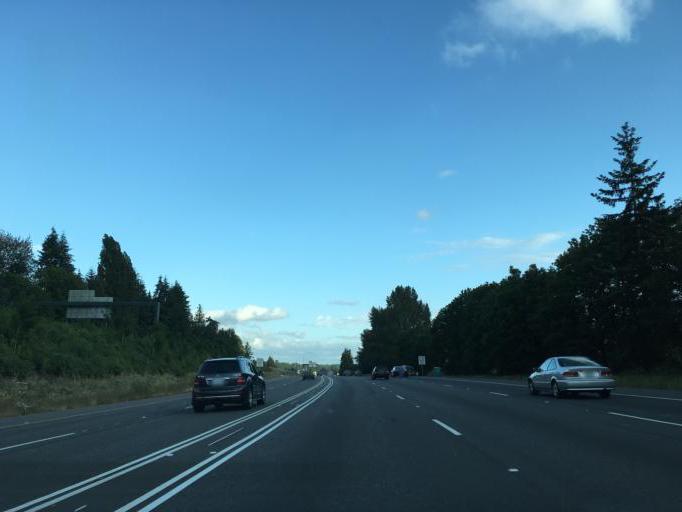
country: US
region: Washington
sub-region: King County
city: Kingsgate
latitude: 47.7220
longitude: -122.1896
